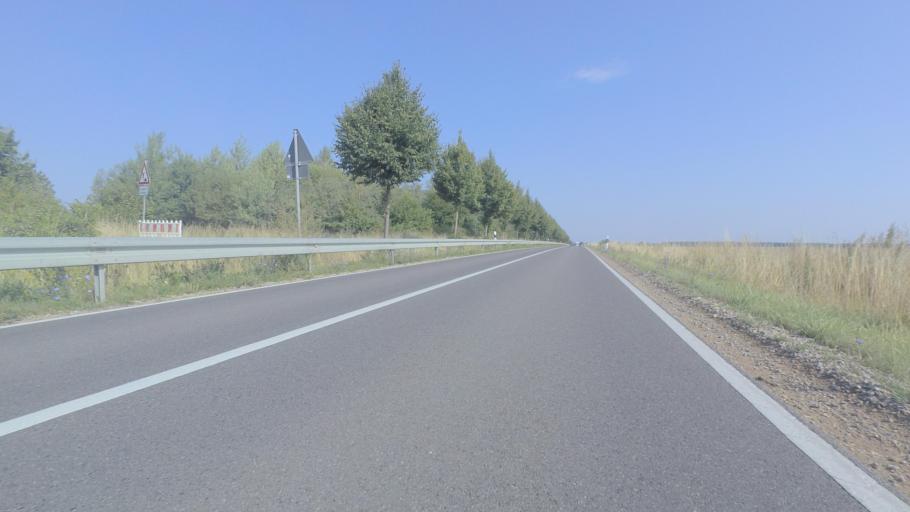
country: DE
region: Mecklenburg-Vorpommern
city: Malchow
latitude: 53.5115
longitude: 12.4230
